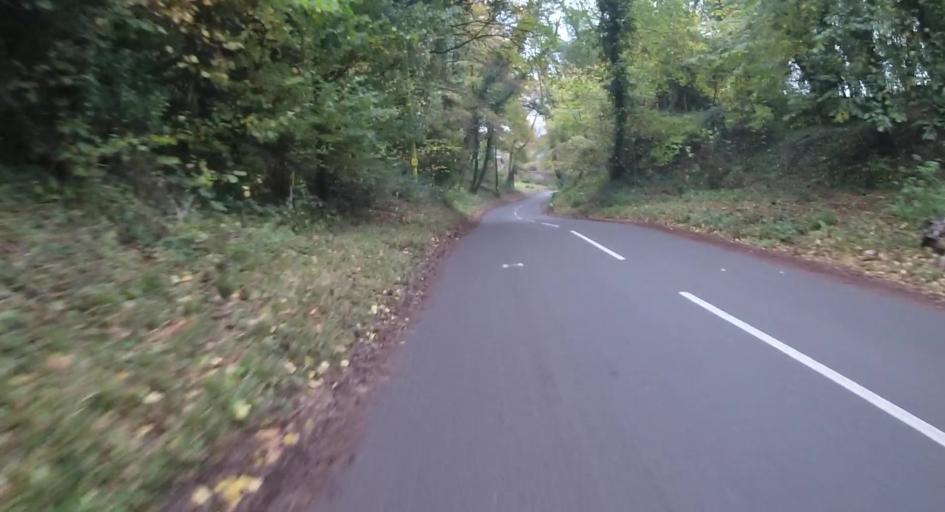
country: GB
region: England
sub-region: Hampshire
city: Kingsley
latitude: 51.1642
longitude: -0.8757
